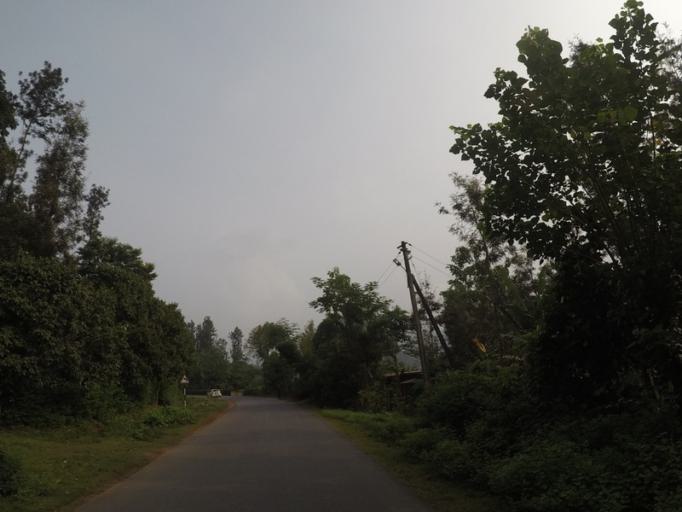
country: IN
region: Karnataka
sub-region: Chikmagalur
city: Chikmagalur
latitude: 13.3433
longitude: 75.5438
